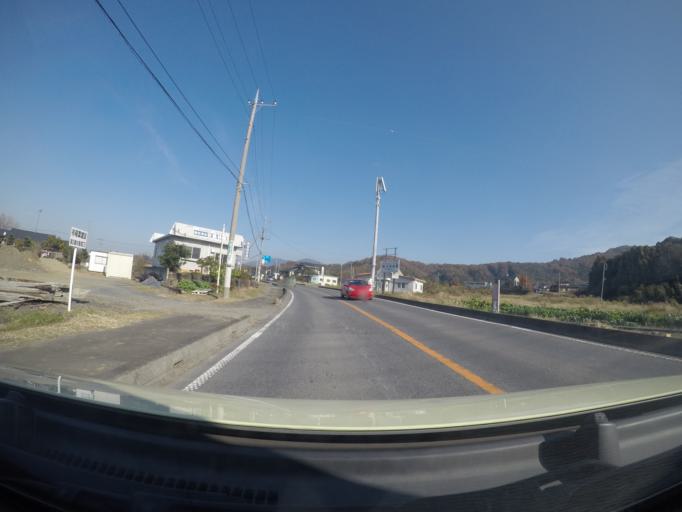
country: JP
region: Ibaraki
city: Makabe
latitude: 36.2586
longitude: 140.0881
